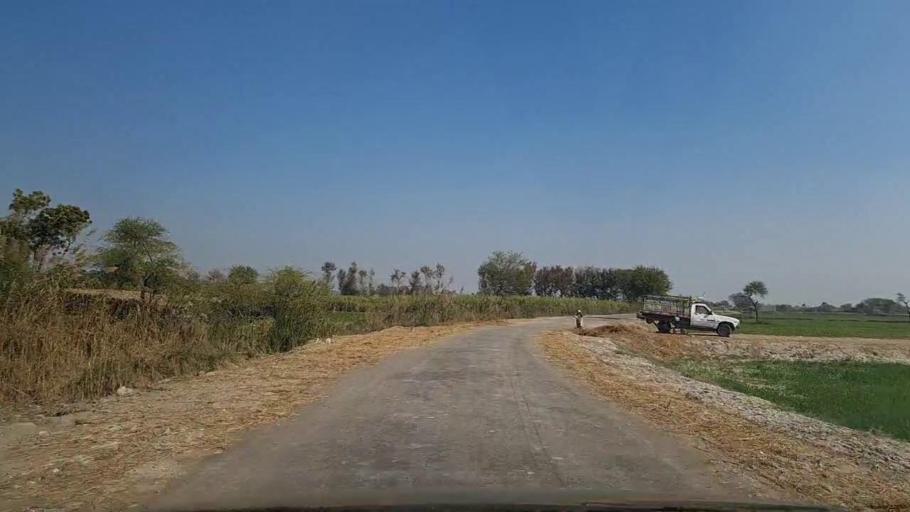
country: PK
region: Sindh
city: Bandhi
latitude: 26.5556
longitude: 68.3486
